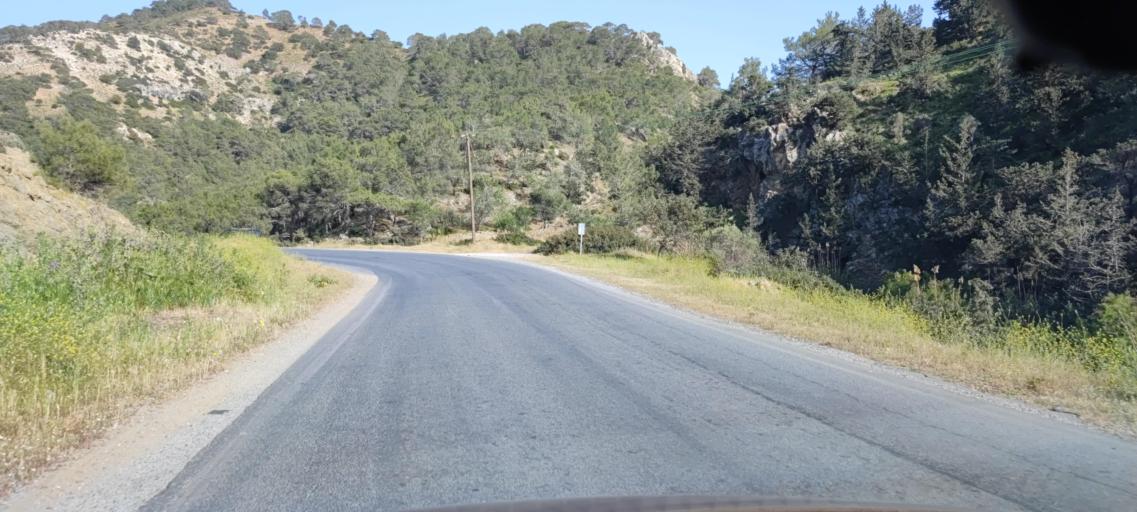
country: CY
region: Keryneia
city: Lapithos
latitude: 35.3396
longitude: 33.0711
